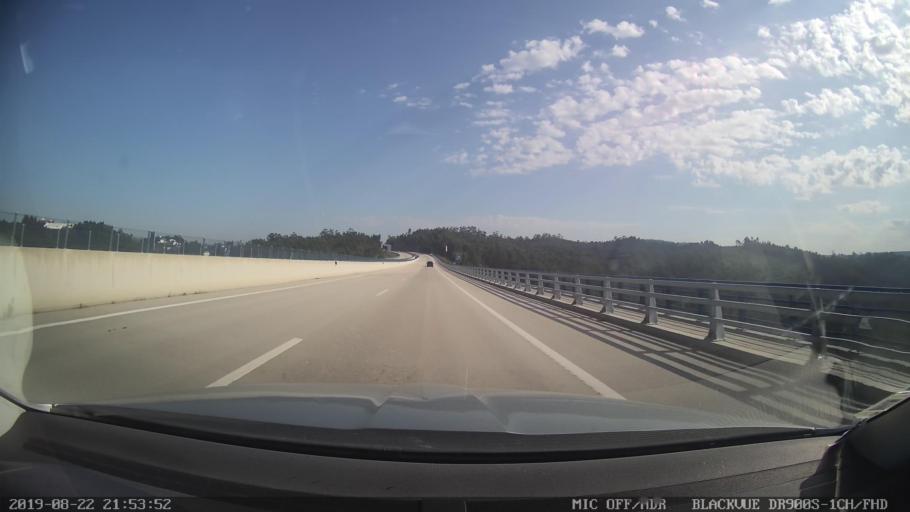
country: PT
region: Coimbra
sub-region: Miranda do Corvo
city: Miranda do Corvo
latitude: 40.1248
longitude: -8.3823
